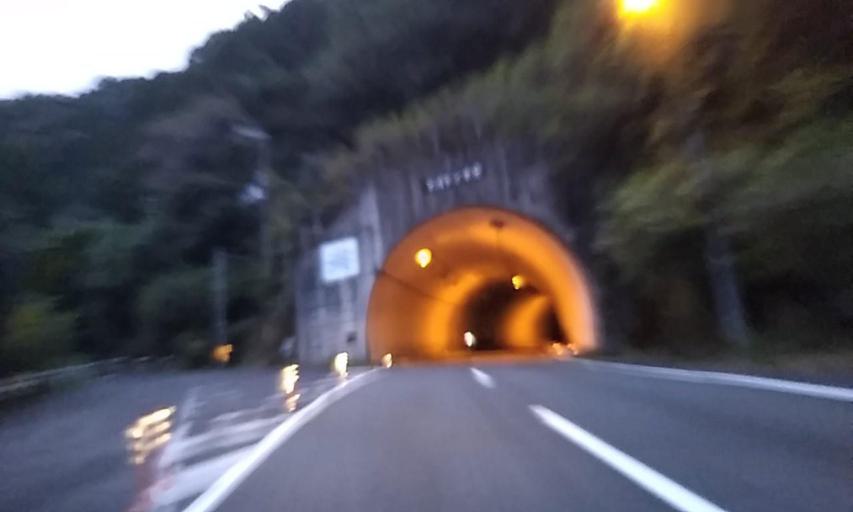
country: JP
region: Wakayama
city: Shingu
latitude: 33.7321
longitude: 135.9231
